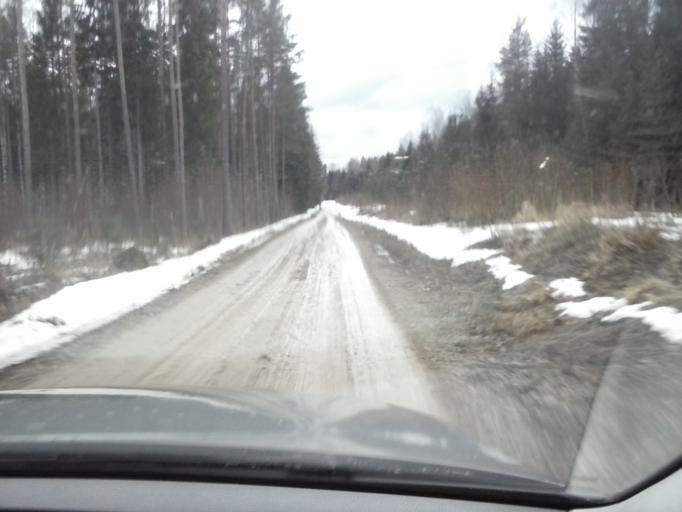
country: EE
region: Ida-Virumaa
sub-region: Johvi vald
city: Johvi
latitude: 59.1746
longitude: 27.3137
